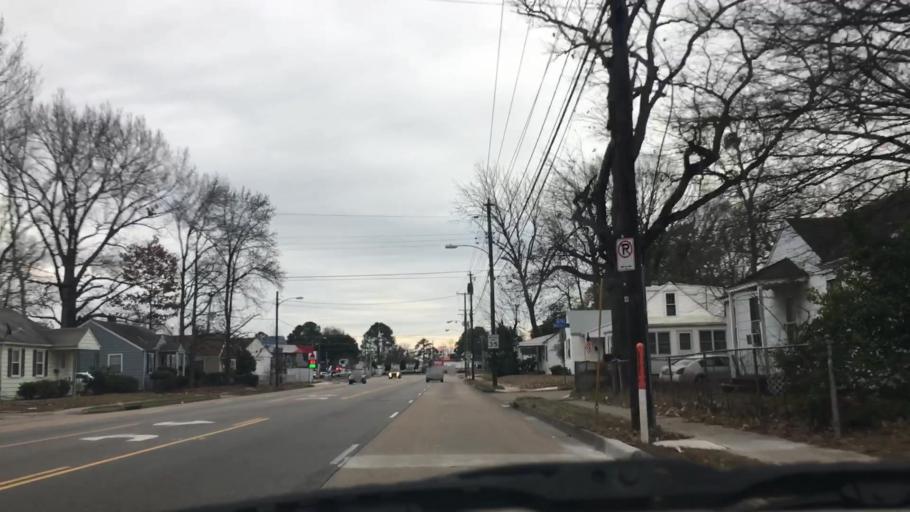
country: US
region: Virginia
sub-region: City of Norfolk
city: Norfolk
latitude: 36.8729
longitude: -76.2325
